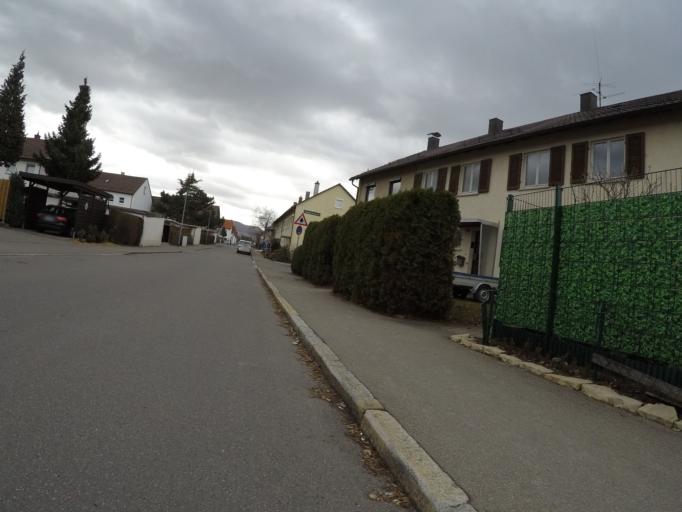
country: DE
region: Baden-Wuerttemberg
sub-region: Tuebingen Region
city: Reutlingen
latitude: 48.5100
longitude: 9.2139
